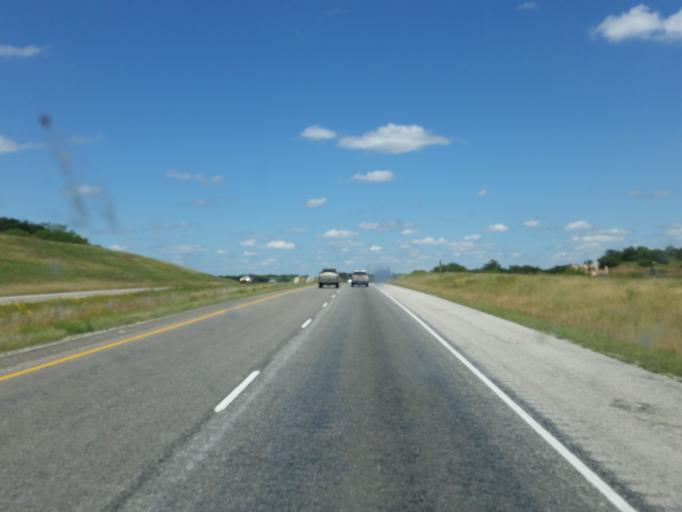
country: US
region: Texas
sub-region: Eastland County
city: Cisco
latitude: 32.3754
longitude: -99.0894
